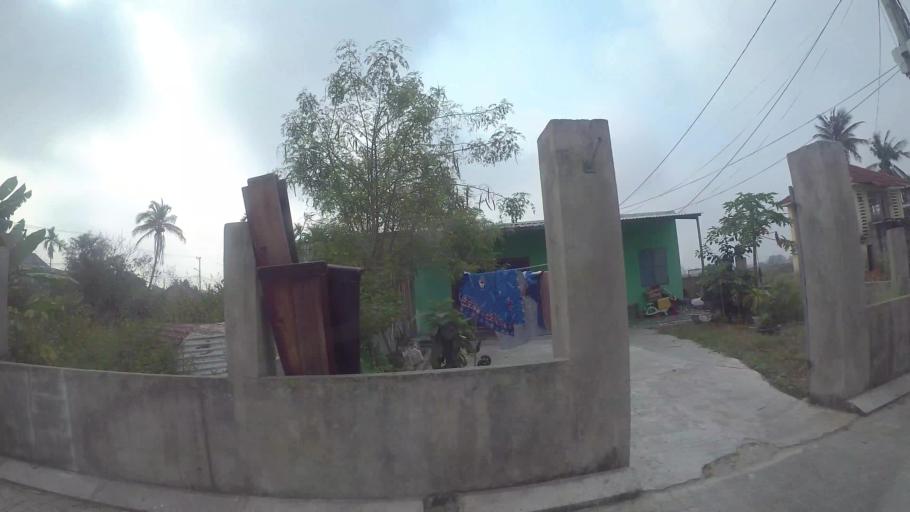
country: VN
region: Da Nang
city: Ngu Hanh Son
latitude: 16.0211
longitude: 108.2434
